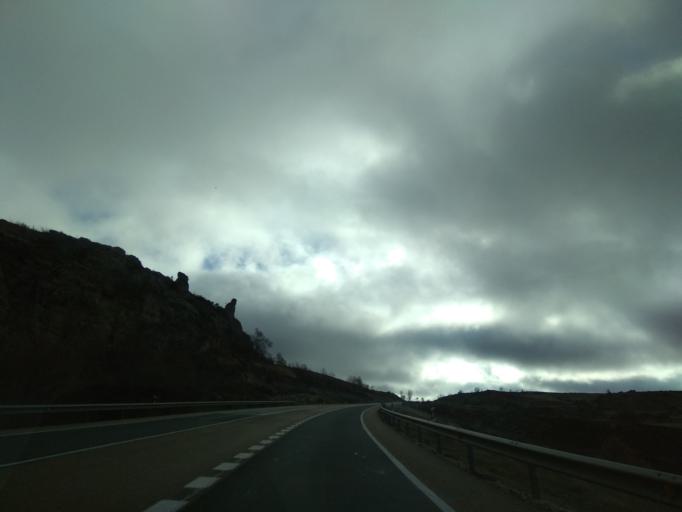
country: ES
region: Castille and Leon
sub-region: Provincia de Burgos
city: Huermeces
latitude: 42.5548
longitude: -3.7473
